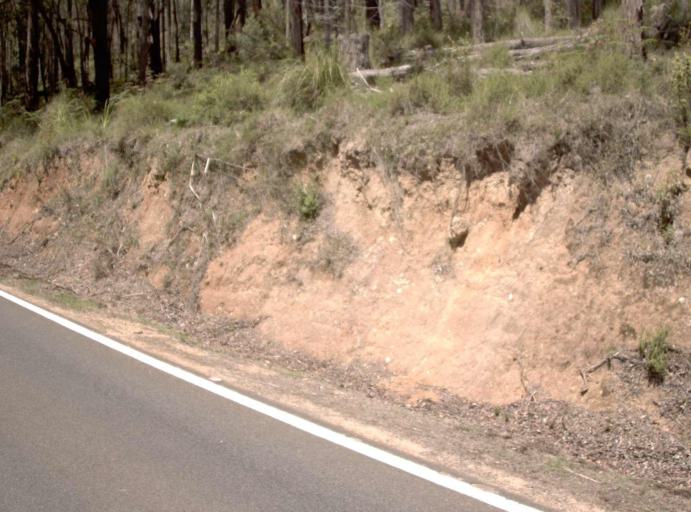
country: AU
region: New South Wales
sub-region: Bombala
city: Bombala
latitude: -37.5942
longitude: 148.9144
